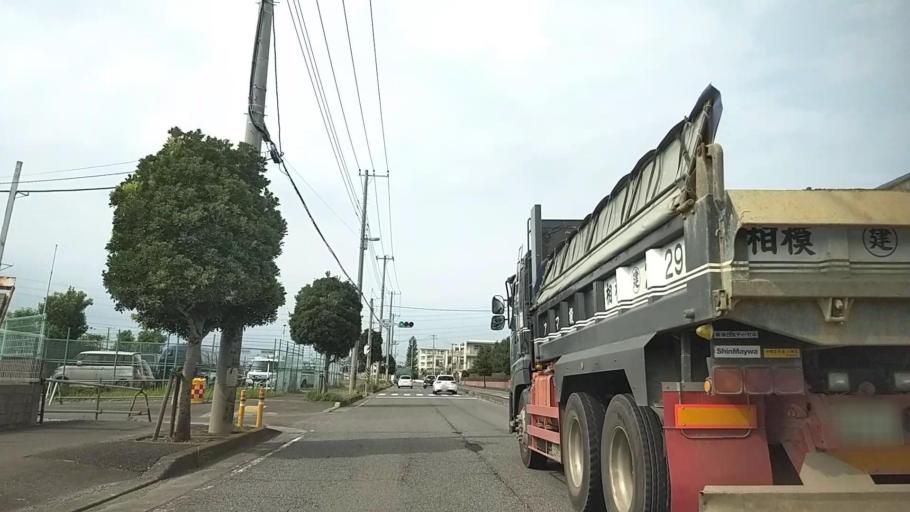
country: JP
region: Kanagawa
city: Atsugi
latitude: 35.4312
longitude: 139.3832
